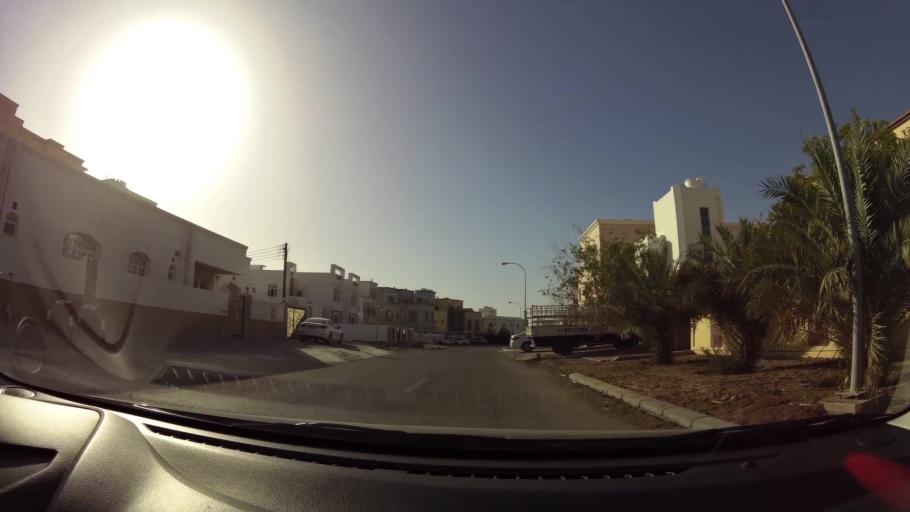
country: OM
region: Muhafazat Masqat
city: As Sib al Jadidah
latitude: 23.5968
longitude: 58.2044
